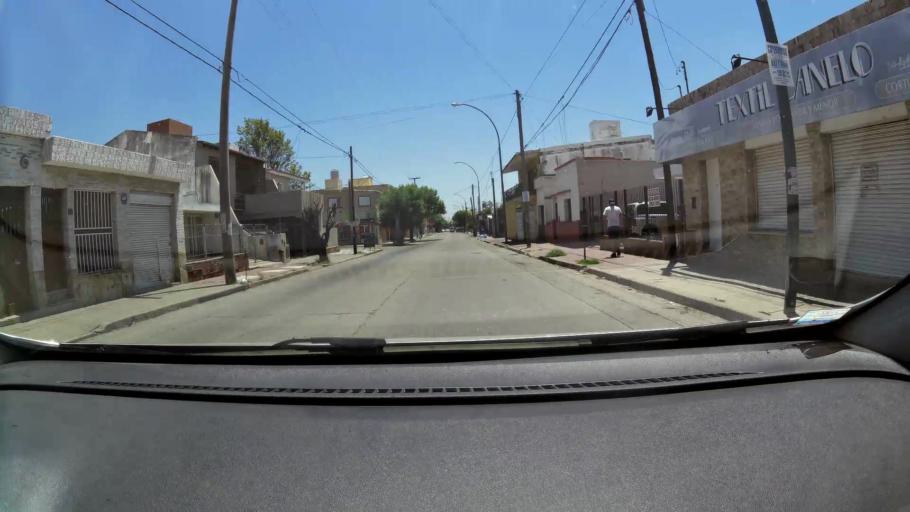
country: AR
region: Cordoba
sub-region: Departamento de Capital
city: Cordoba
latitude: -31.4109
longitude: -64.2251
